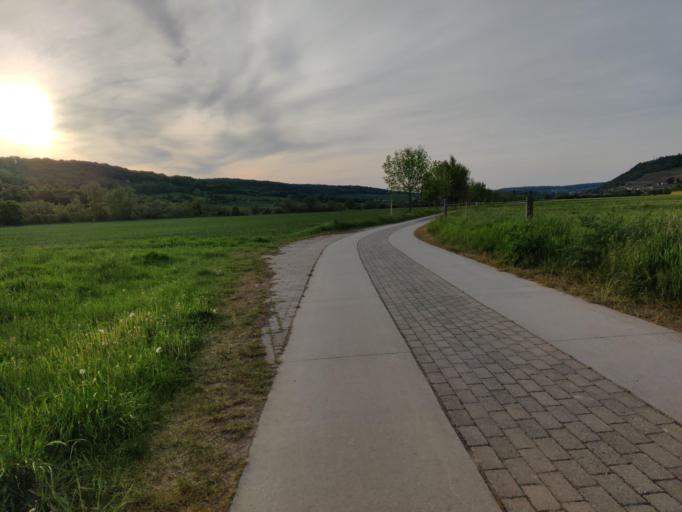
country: DE
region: Saxony-Anhalt
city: Freyburg
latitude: 51.1906
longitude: 11.7816
